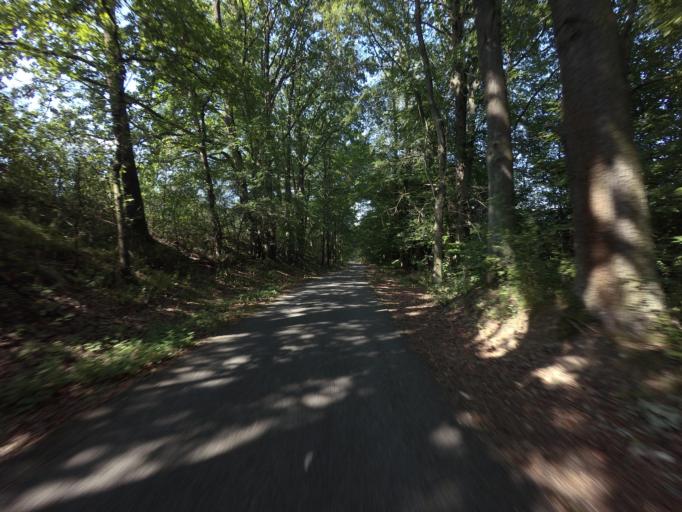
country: CZ
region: Jihocesky
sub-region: Okres Ceske Budejovice
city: Hluboka nad Vltavou
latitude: 49.1175
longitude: 14.4583
